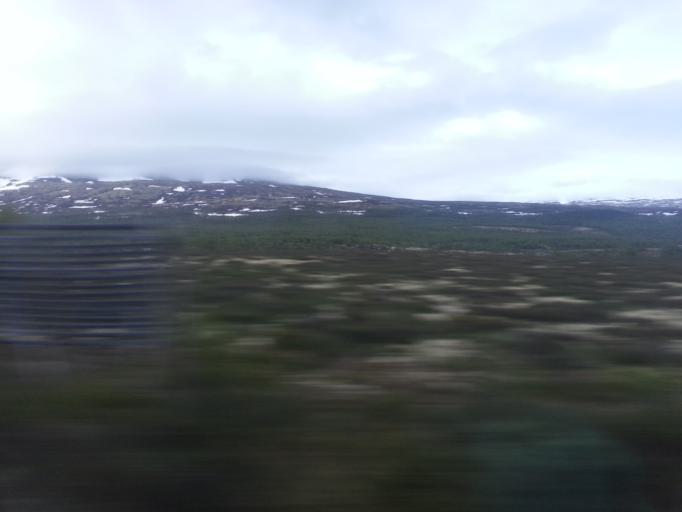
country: NO
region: Oppland
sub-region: Dovre
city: Dovre
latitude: 62.1311
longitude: 9.2933
